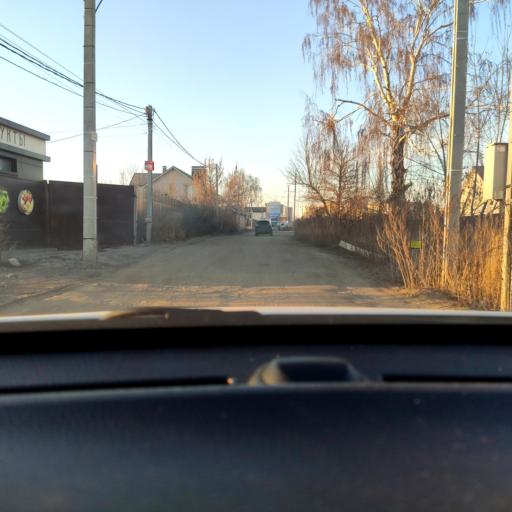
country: RU
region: Voronezj
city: Somovo
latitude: 51.6757
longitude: 39.3332
